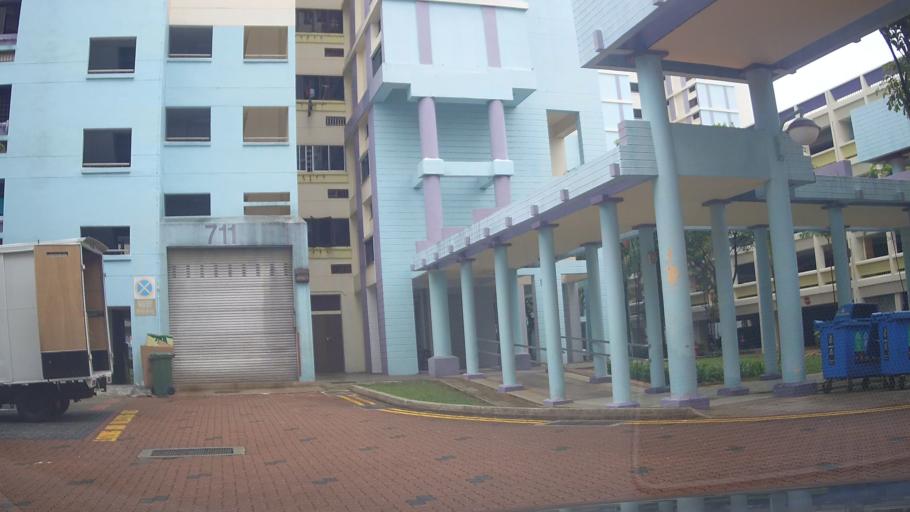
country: MY
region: Johor
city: Johor Bahru
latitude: 1.4410
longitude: 103.7976
